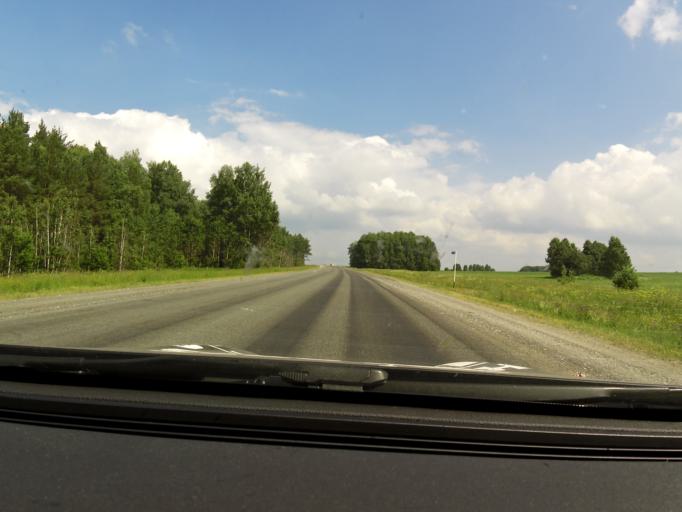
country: RU
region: Sverdlovsk
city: Ufimskiy
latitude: 56.7720
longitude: 58.0331
